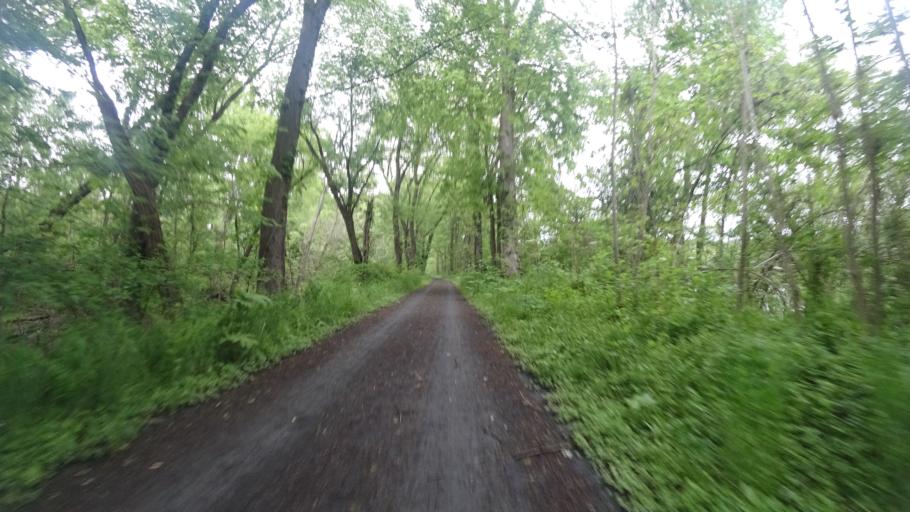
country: US
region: Maryland
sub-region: Frederick County
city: Brunswick
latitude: 39.3054
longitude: -77.6042
